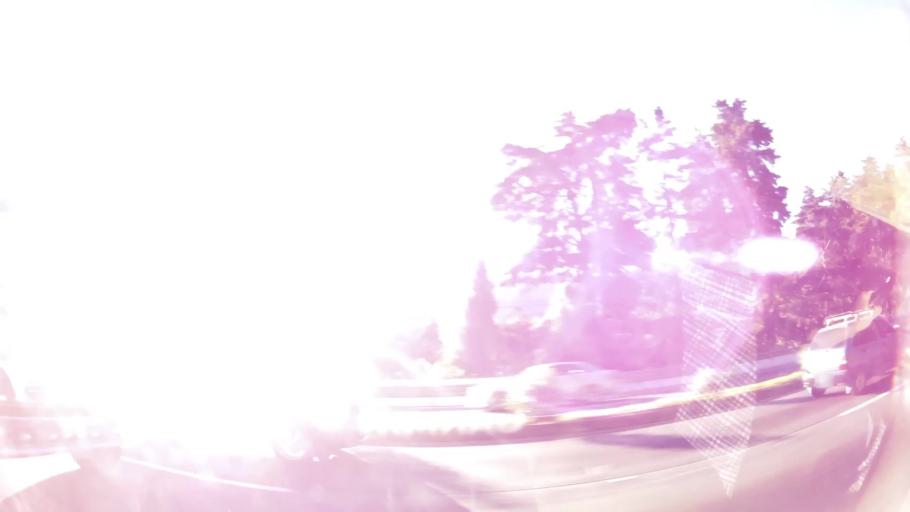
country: GT
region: Sacatepequez
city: San Lucas Sacatepequez
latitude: 14.6059
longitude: -90.6271
